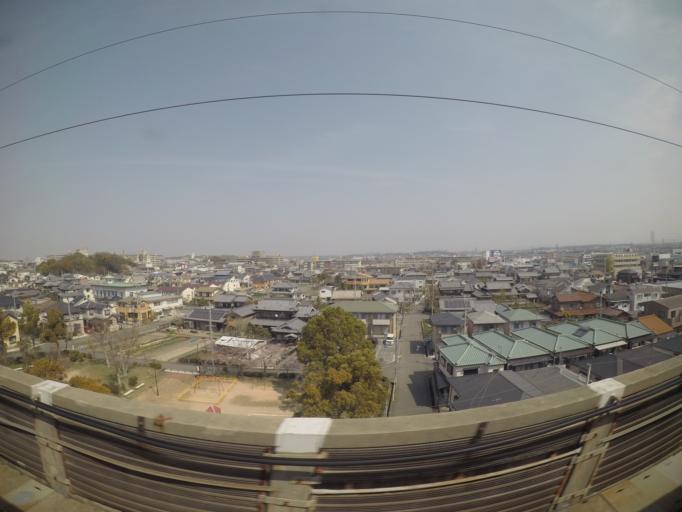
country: JP
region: Hyogo
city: Akashi
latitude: 34.6658
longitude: 134.9774
